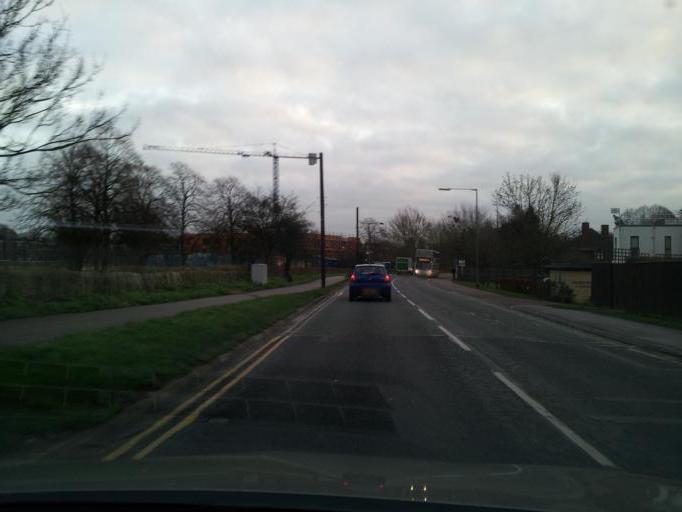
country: GB
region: England
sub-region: Cambridgeshire
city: Cambridge
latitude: 52.2120
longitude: 0.0981
